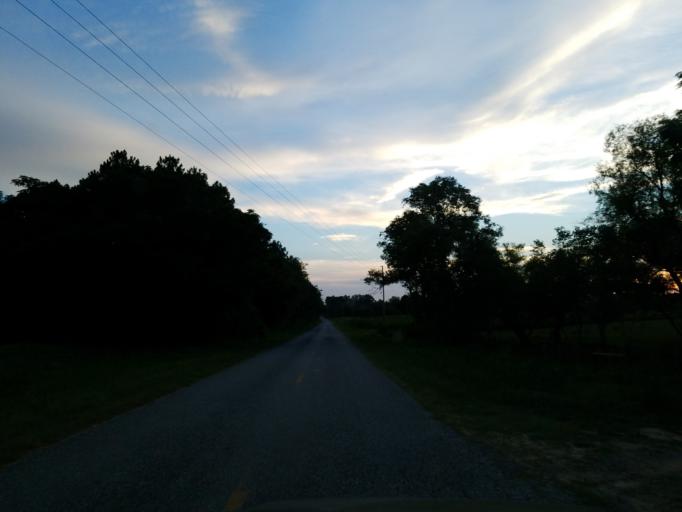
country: US
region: Georgia
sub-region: Crisp County
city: Cordele
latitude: 31.8370
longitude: -83.7585
